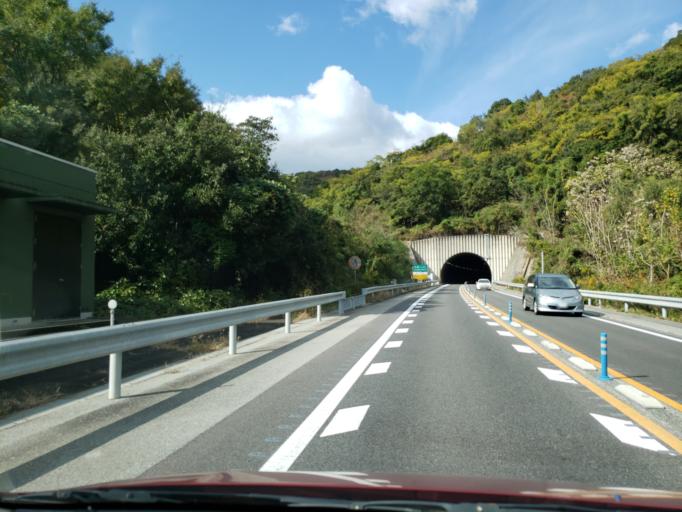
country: JP
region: Tokushima
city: Kamojimacho-jogejima
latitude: 34.1050
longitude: 134.2953
